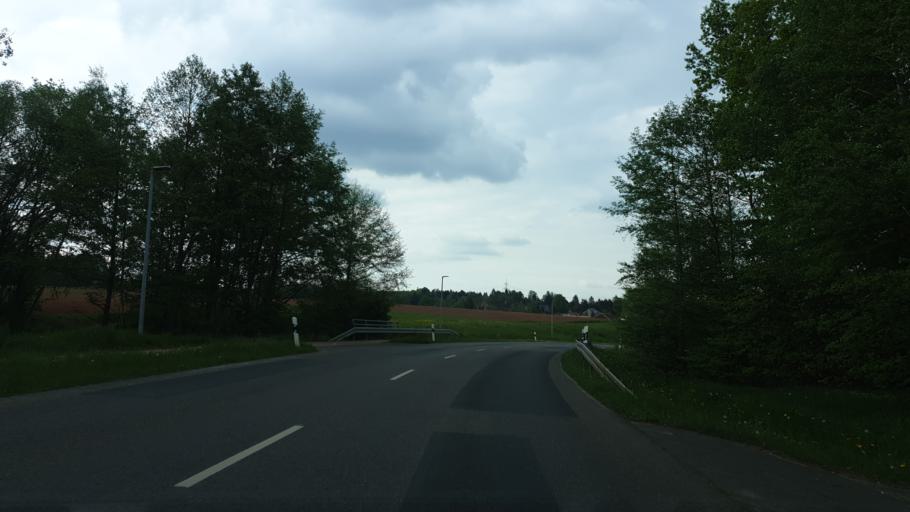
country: DE
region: Saxony
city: Neukirchen
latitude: 50.7699
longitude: 12.8737
